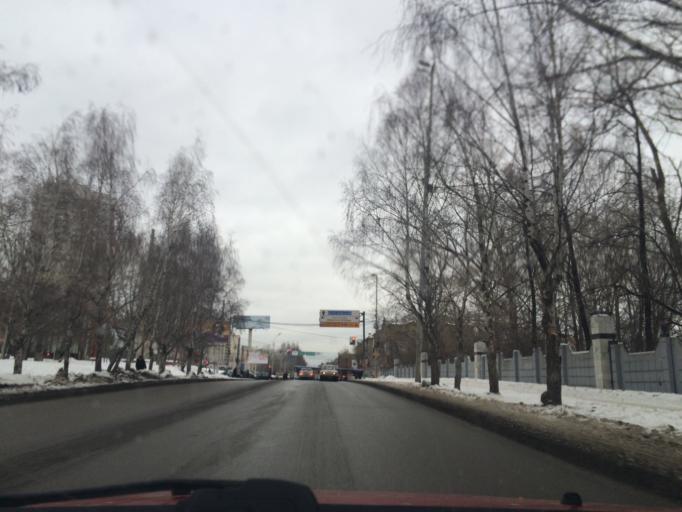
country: RU
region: Sverdlovsk
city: Yekaterinburg
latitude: 56.8504
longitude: 60.6392
